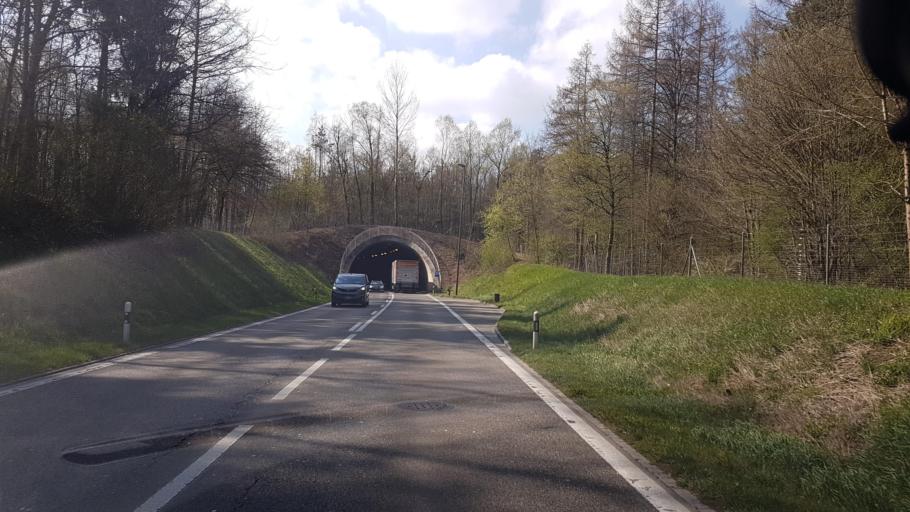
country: CH
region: Aargau
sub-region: Bezirk Bremgarten
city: Bremgarten
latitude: 47.3609
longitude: 8.3411
